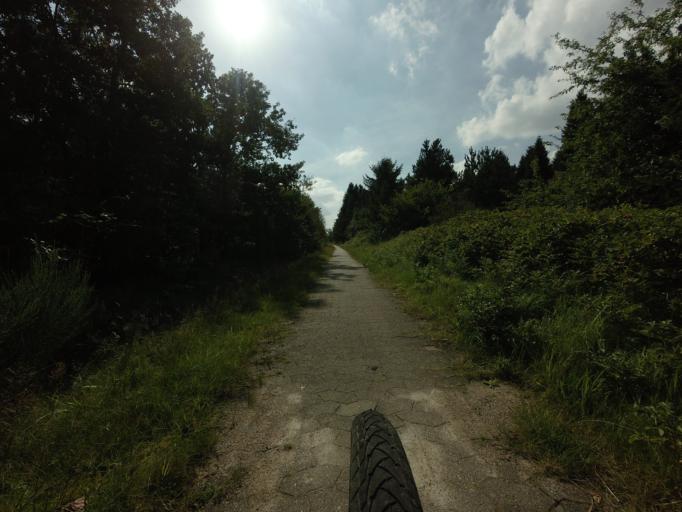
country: DK
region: Central Jutland
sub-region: Viborg Kommune
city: Karup
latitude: 56.2766
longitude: 9.1208
